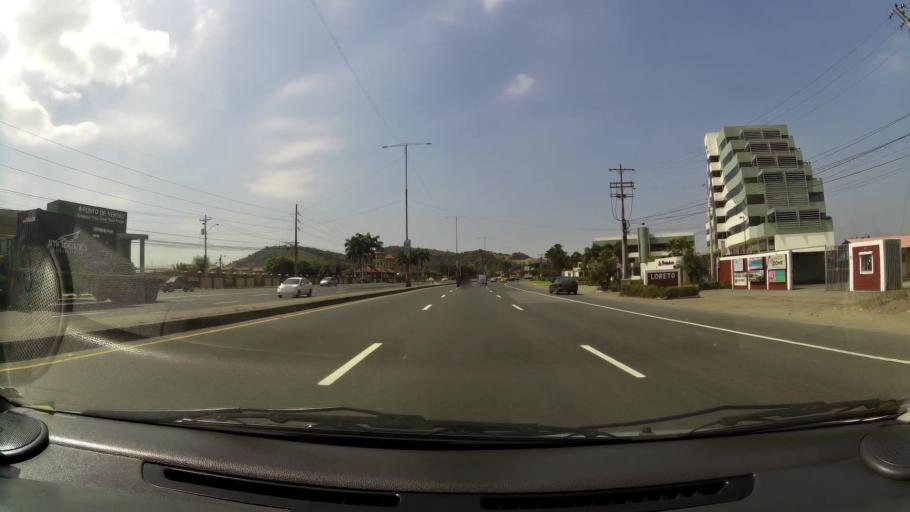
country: EC
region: Guayas
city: El Triunfo
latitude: -2.0508
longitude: -79.9137
